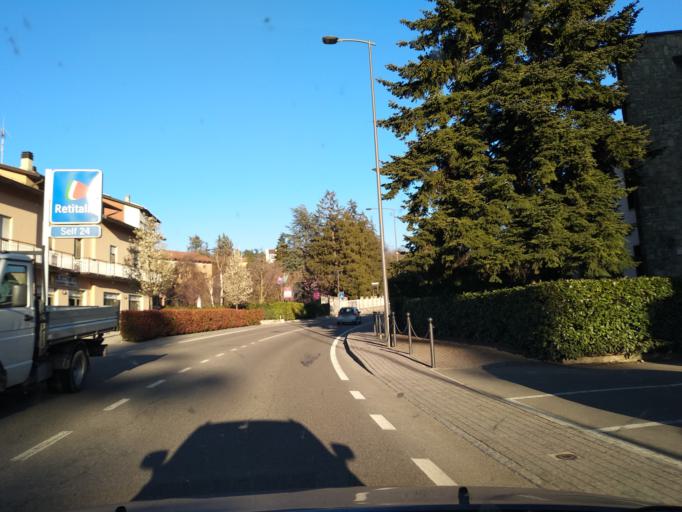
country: IT
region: Emilia-Romagna
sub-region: Provincia di Reggio Emilia
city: Castelnovo ne'Monti
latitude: 44.4340
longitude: 10.4057
